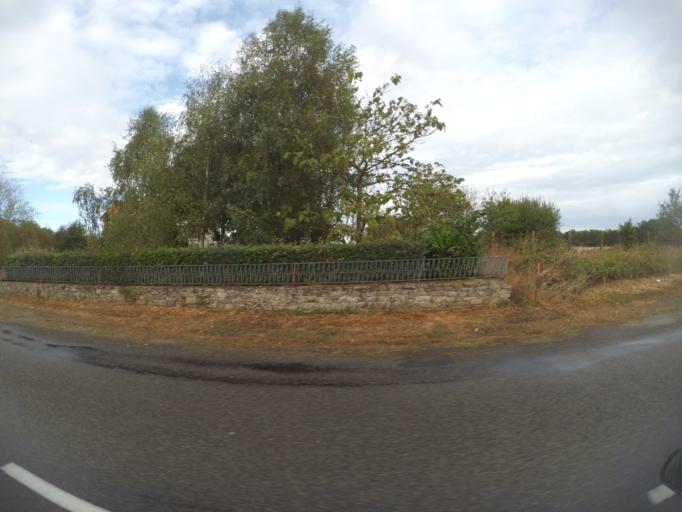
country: FR
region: Pays de la Loire
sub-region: Departement de la Loire-Atlantique
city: Aigrefeuille-sur-Maine
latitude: 47.0529
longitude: -1.4128
